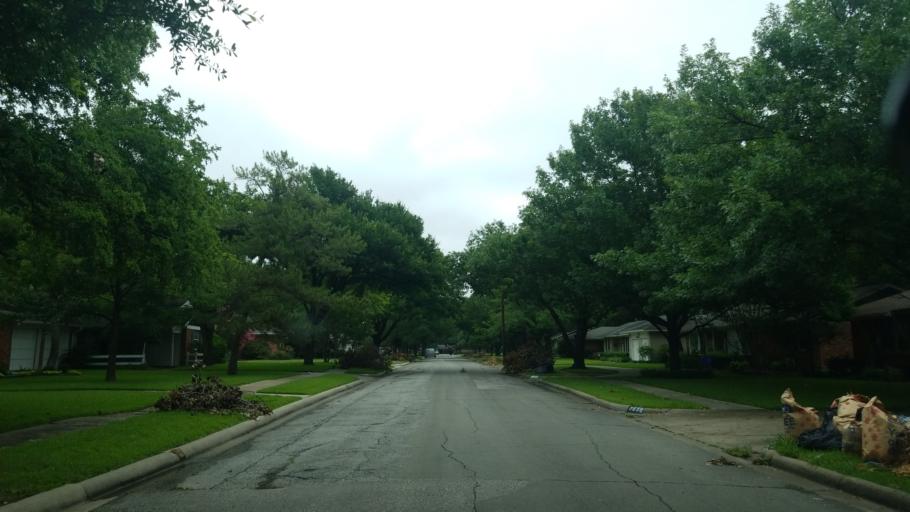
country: US
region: Texas
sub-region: Dallas County
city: Farmers Branch
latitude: 32.8961
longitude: -96.8684
